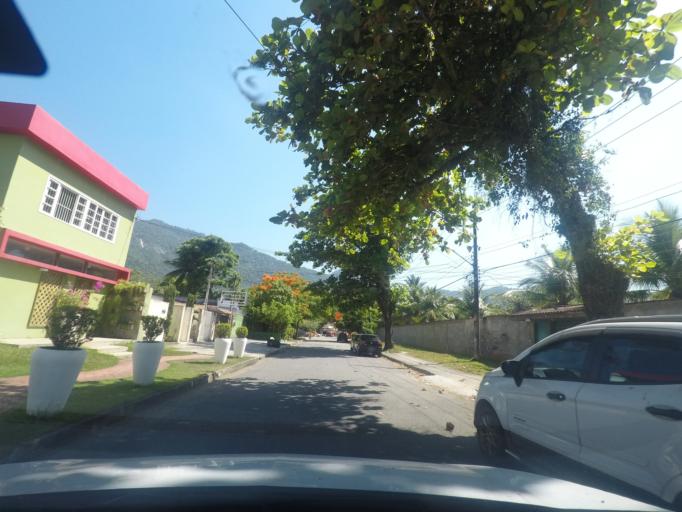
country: BR
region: Rio de Janeiro
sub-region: Nilopolis
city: Nilopolis
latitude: -22.9859
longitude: -43.4567
